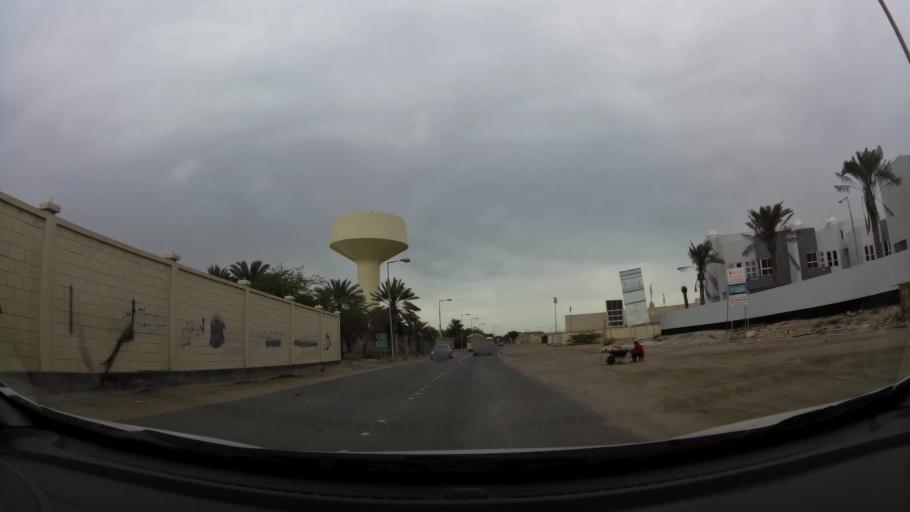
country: BH
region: Central Governorate
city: Madinat Hamad
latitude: 26.1400
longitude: 50.4602
